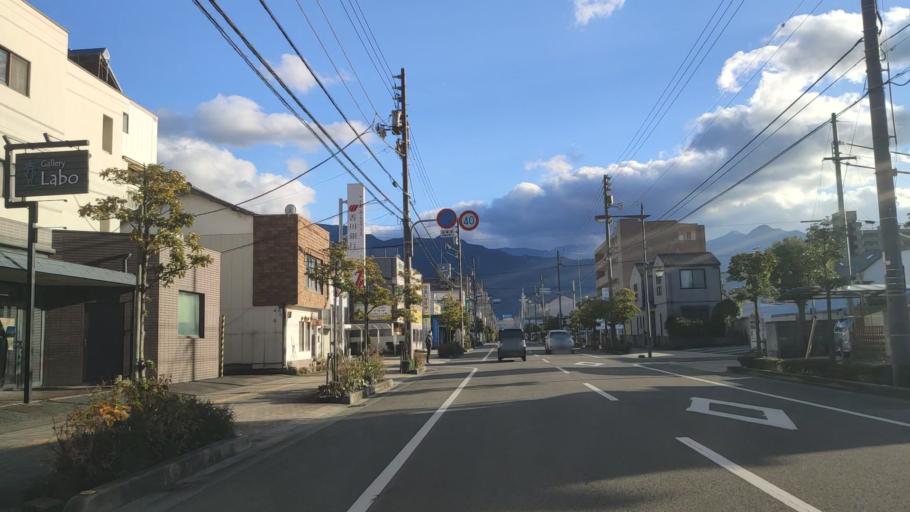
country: JP
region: Ehime
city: Saijo
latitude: 33.9173
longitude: 133.1859
